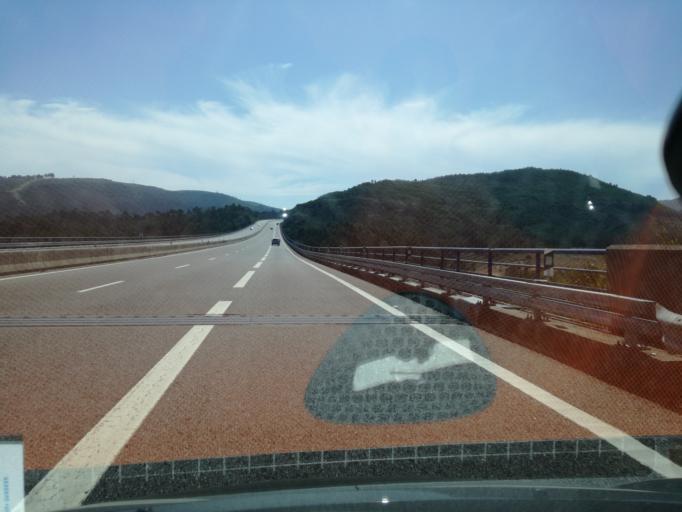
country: PT
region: Viana do Castelo
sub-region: Caminha
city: Vila Praia de Ancora
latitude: 41.8014
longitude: -8.8004
